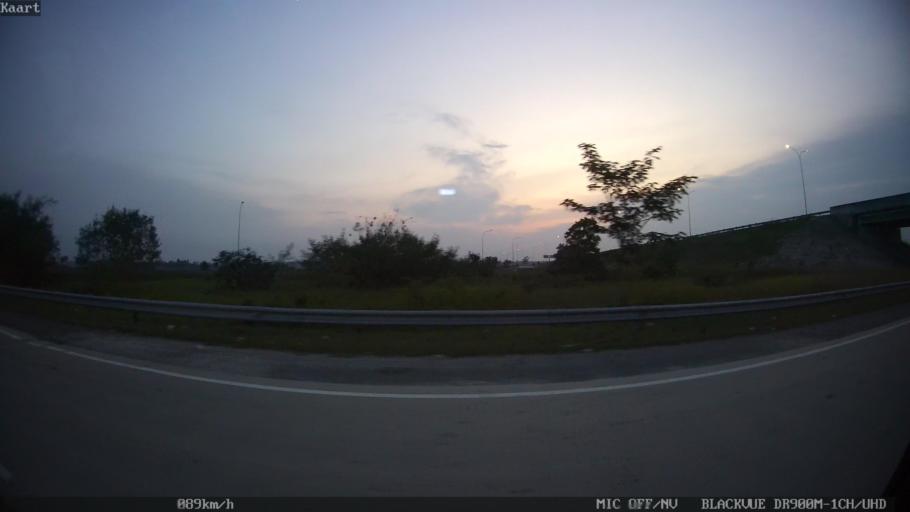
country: ID
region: Lampung
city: Sidorejo
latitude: -5.6086
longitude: 105.5570
